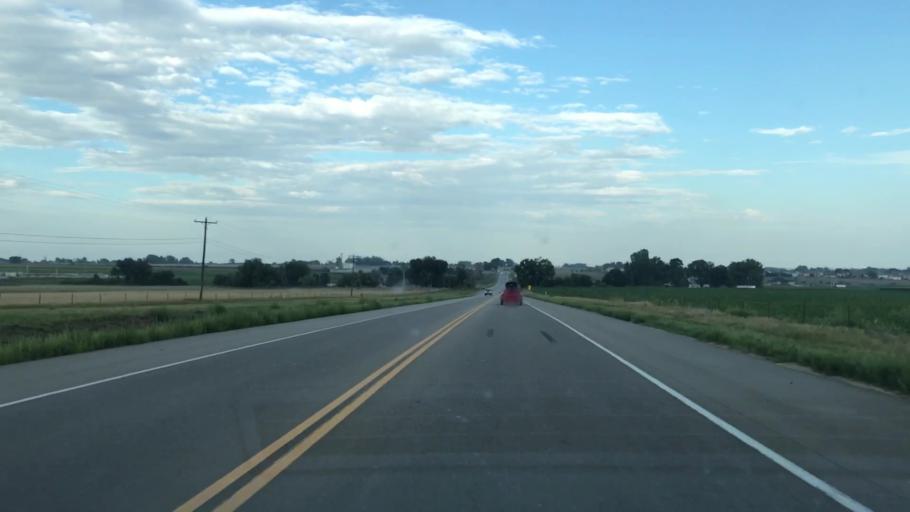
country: US
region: Colorado
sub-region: Weld County
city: Mead
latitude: 40.2039
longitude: -105.0241
